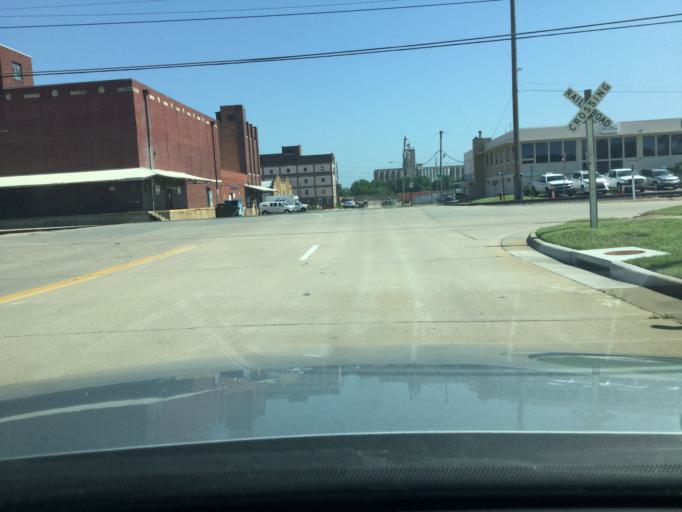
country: US
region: Kansas
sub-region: Shawnee County
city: Topeka
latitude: 39.0580
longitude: -95.6689
